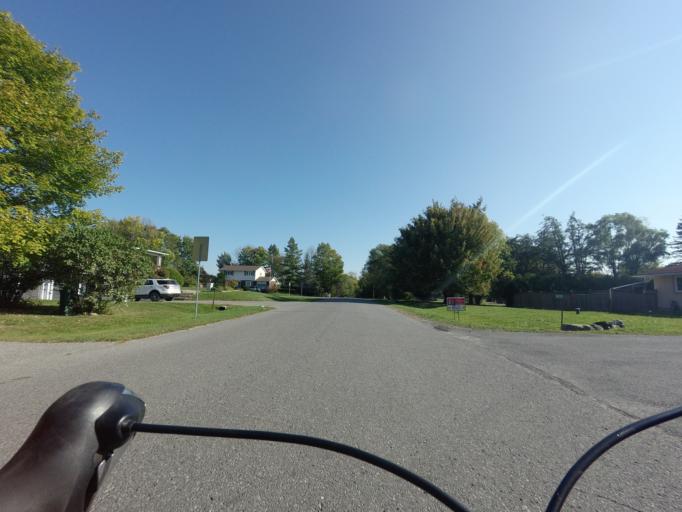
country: CA
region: Ontario
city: Bells Corners
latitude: 45.2227
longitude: -75.6737
